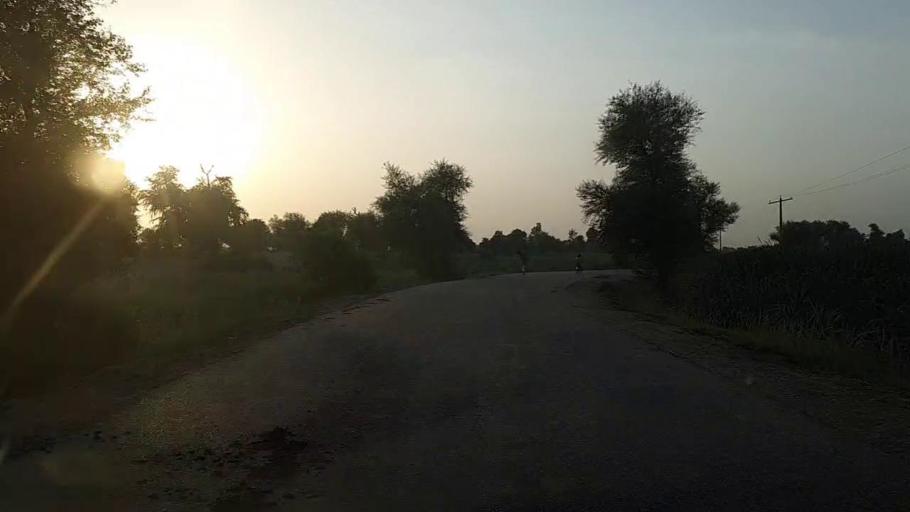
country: PK
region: Sindh
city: Ubauro
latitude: 28.2225
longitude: 69.8200
